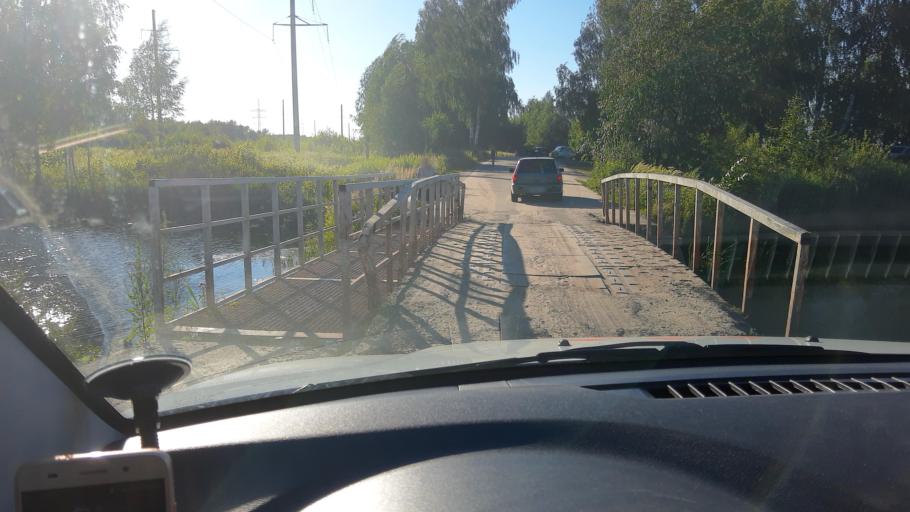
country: RU
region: Nizjnij Novgorod
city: Gorbatovka
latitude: 56.3633
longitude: 43.7847
